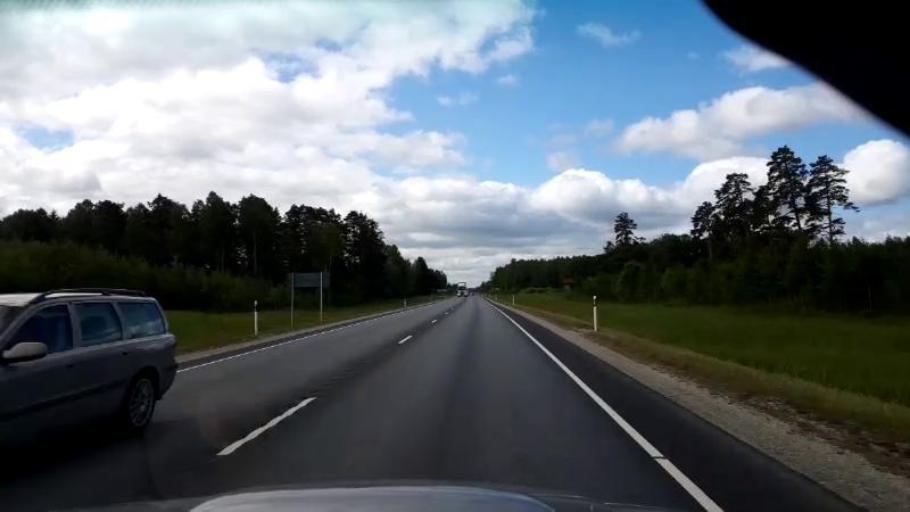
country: EE
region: Harju
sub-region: Nissi vald
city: Riisipere
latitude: 59.0720
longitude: 24.4524
